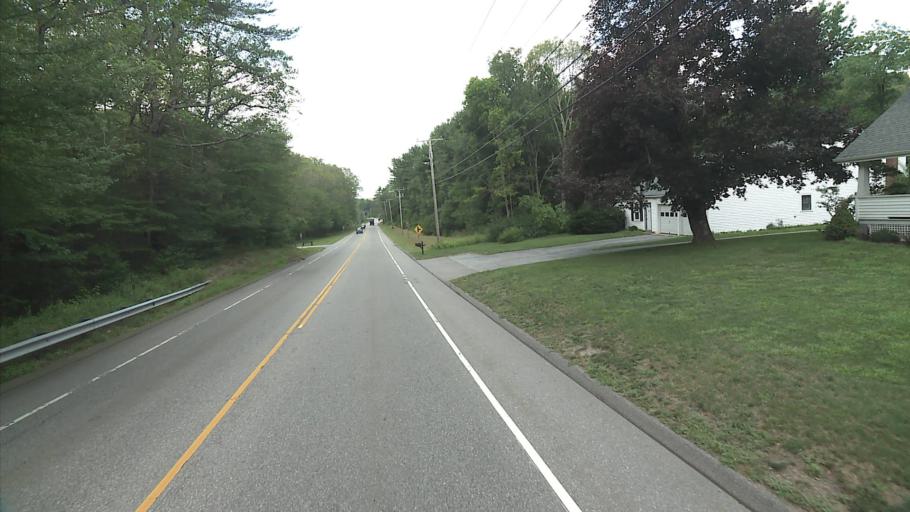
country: US
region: Connecticut
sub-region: New London County
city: Jewett City
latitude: 41.5852
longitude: -71.9287
